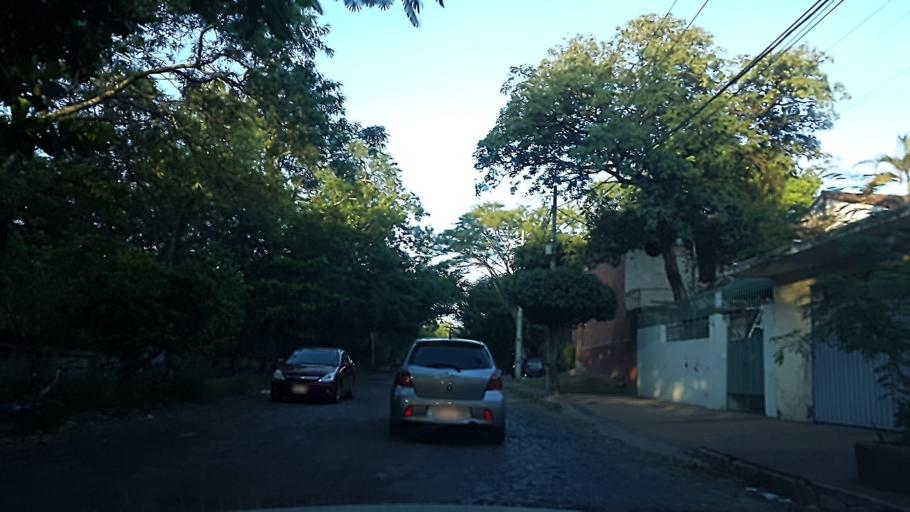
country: PY
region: Asuncion
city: Asuncion
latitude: -25.2693
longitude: -57.5971
